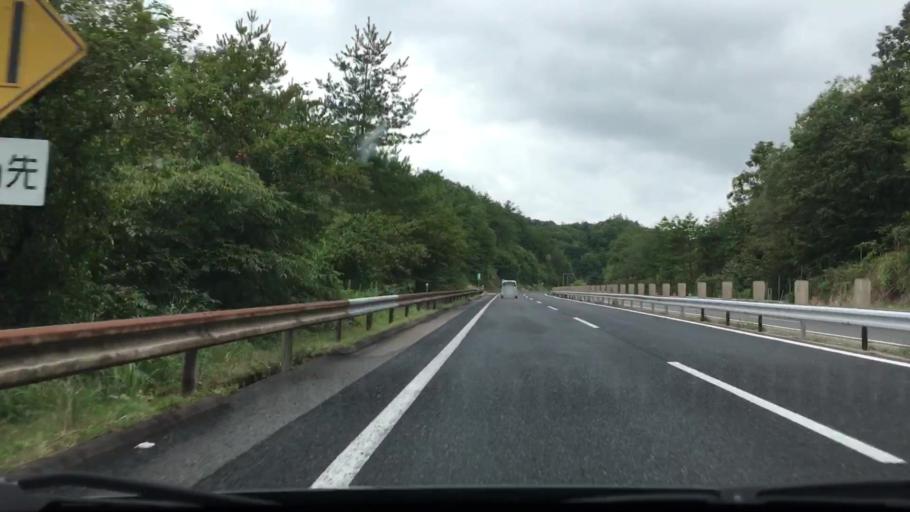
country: JP
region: Hiroshima
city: Miyoshi
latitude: 34.7377
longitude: 132.7123
